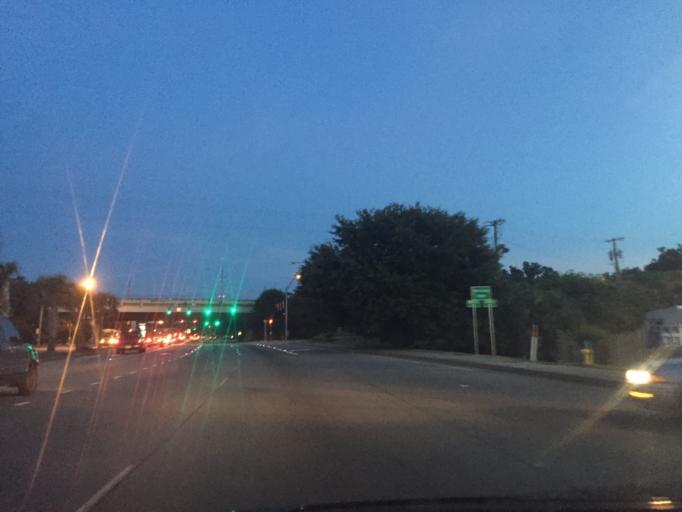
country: US
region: Georgia
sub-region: Chatham County
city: Thunderbolt
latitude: 32.0434
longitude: -81.0682
